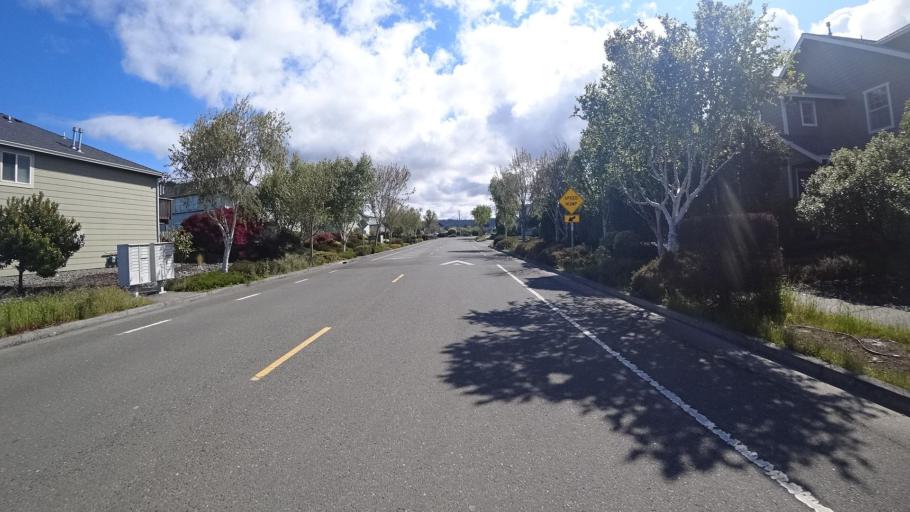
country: US
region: California
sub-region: Humboldt County
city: McKinleyville
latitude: 40.9391
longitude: -124.1047
